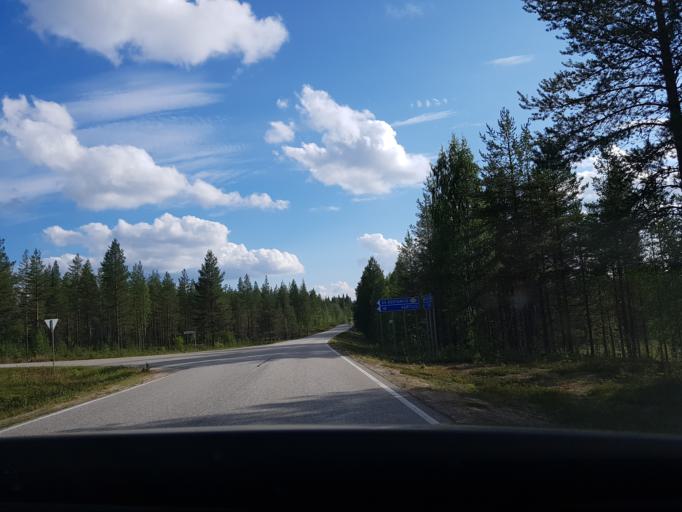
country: FI
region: Kainuu
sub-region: Kehys-Kainuu
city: Kuhmo
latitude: 64.6218
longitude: 29.6978
